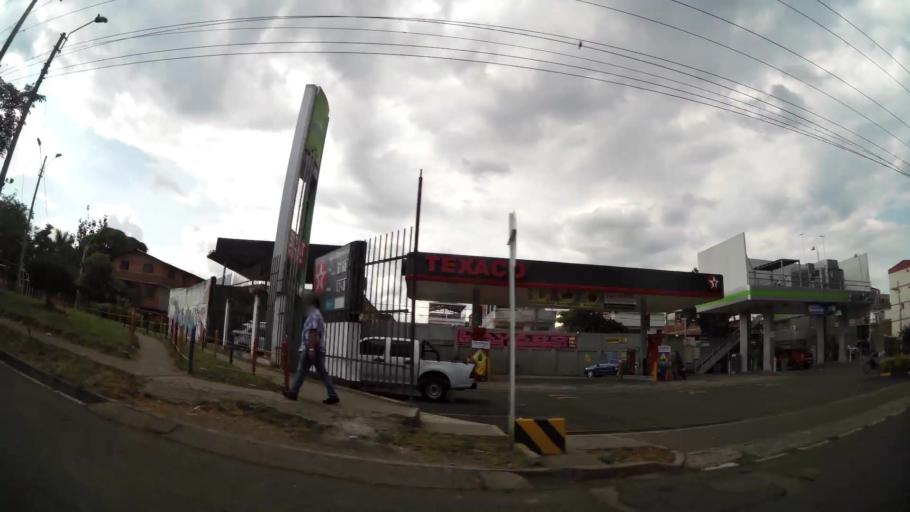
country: CO
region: Valle del Cauca
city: Cali
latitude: 3.4744
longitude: -76.4948
